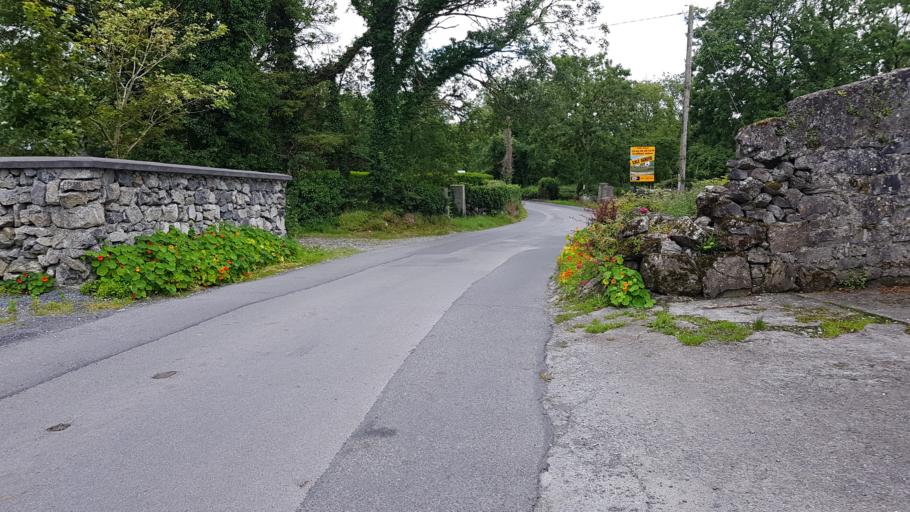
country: IE
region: Connaught
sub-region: County Galway
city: Gaillimh
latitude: 53.2984
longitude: -9.0215
